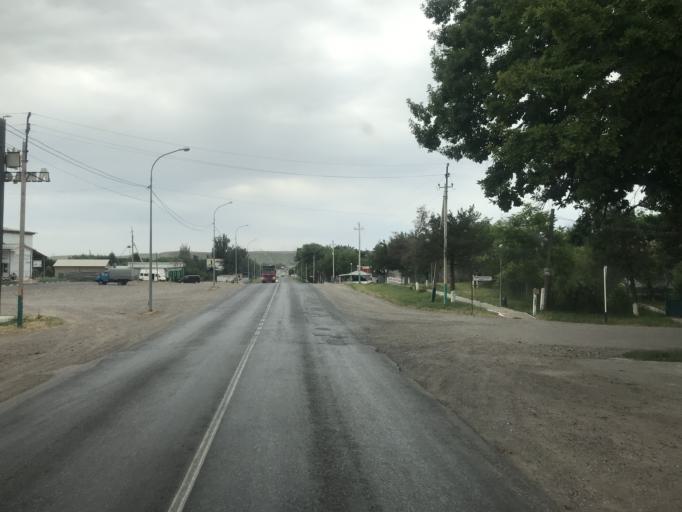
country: KZ
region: Ongtustik Qazaqstan
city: Saryaghash
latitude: 41.4906
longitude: 69.2727
